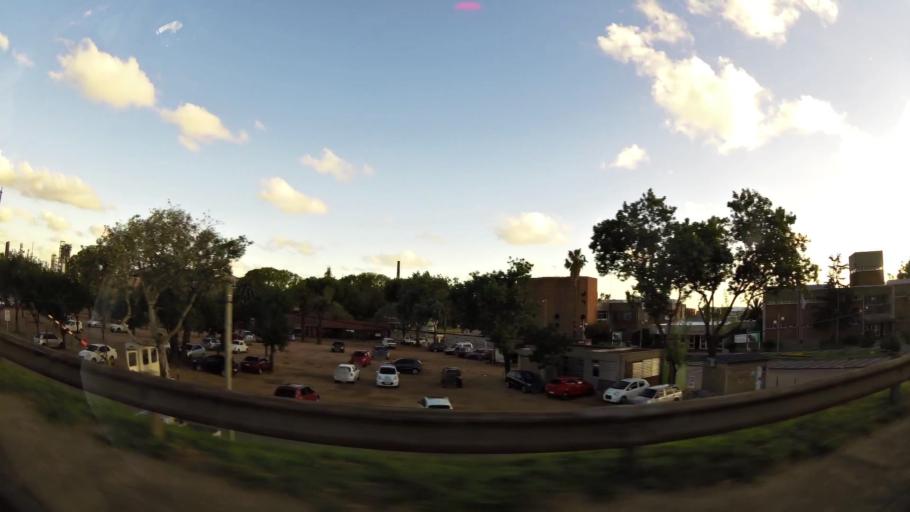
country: UY
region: Montevideo
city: Montevideo
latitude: -34.8720
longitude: -56.2319
